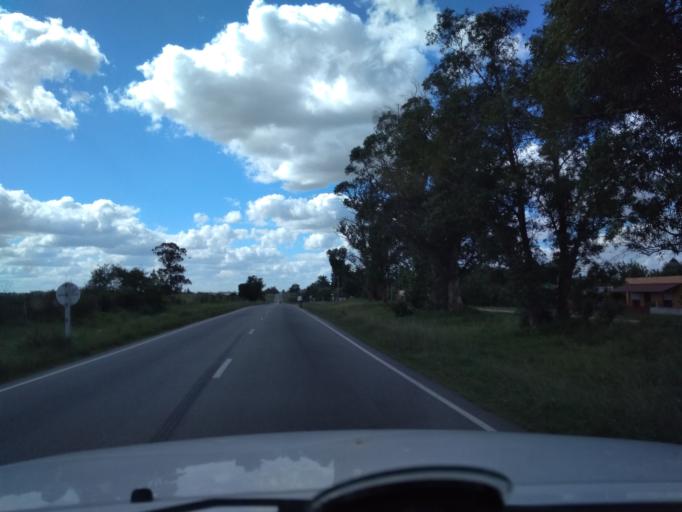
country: UY
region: Canelones
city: Joaquin Suarez
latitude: -34.7094
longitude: -56.0590
